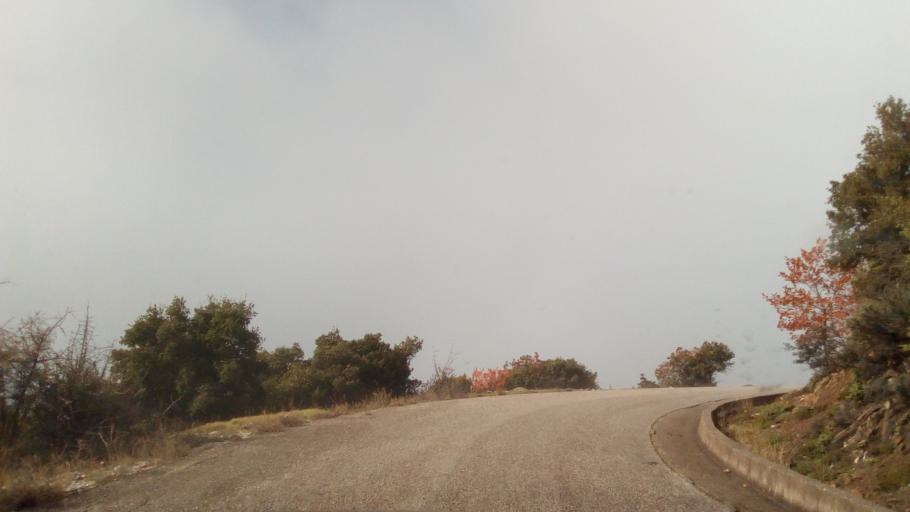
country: GR
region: West Greece
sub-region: Nomos Aitolias kai Akarnanias
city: Nafpaktos
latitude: 38.5377
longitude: 21.9267
